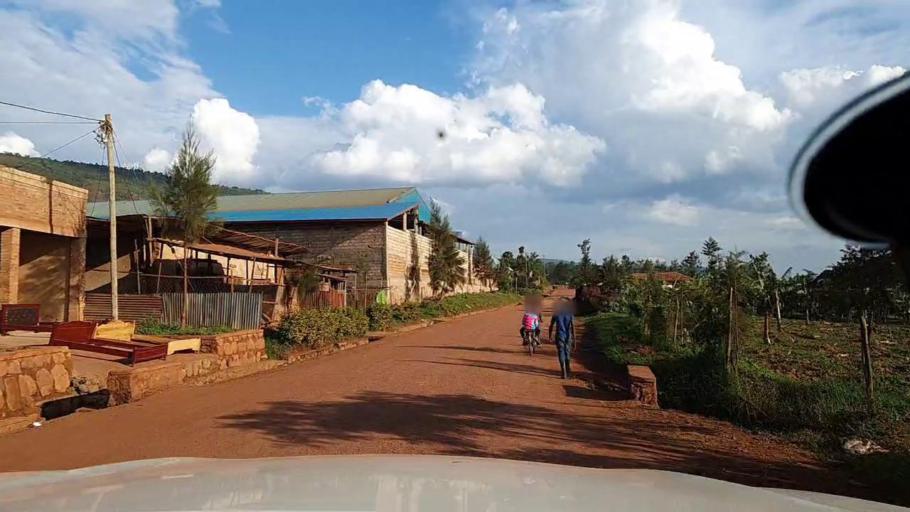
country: RW
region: Kigali
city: Kigali
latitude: -1.9111
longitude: 29.9831
